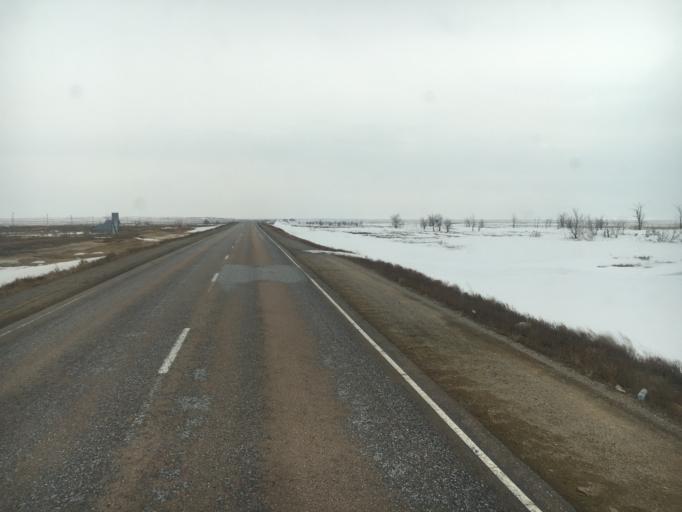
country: RU
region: Orenburg
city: Dombarovskiy
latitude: 50.0936
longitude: 59.4904
